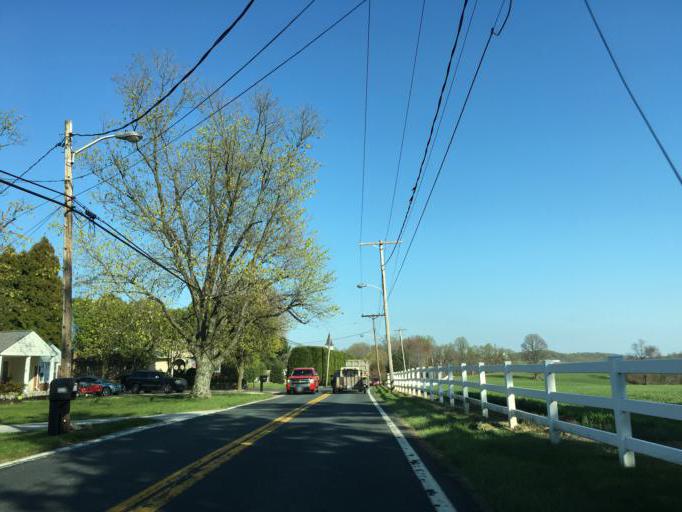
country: US
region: Maryland
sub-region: Baltimore County
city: Perry Hall
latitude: 39.4392
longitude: -76.4923
